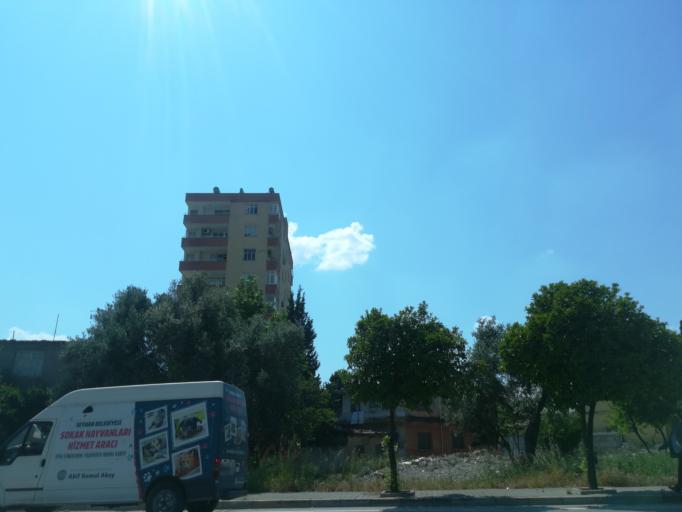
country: TR
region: Adana
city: Adana
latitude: 37.0102
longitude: 35.3372
